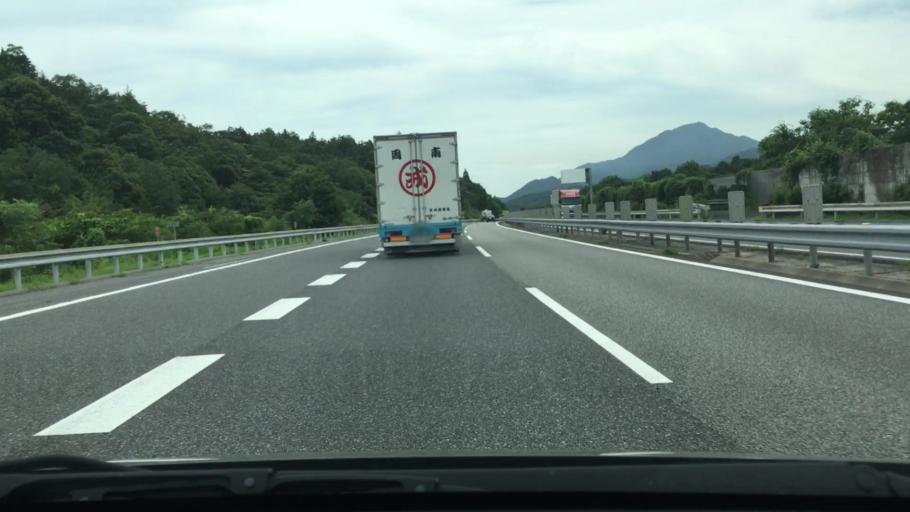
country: JP
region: Hiroshima
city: Miyajima
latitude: 34.3277
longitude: 132.2926
